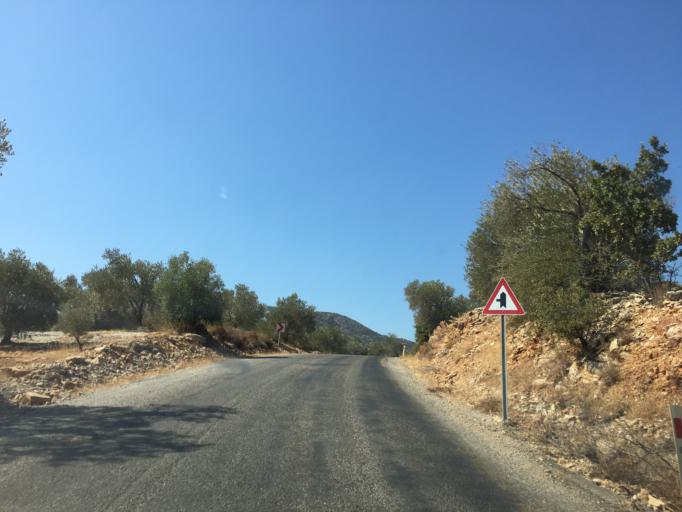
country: TR
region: Mugla
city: Datca
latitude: 36.6952
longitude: 27.4734
